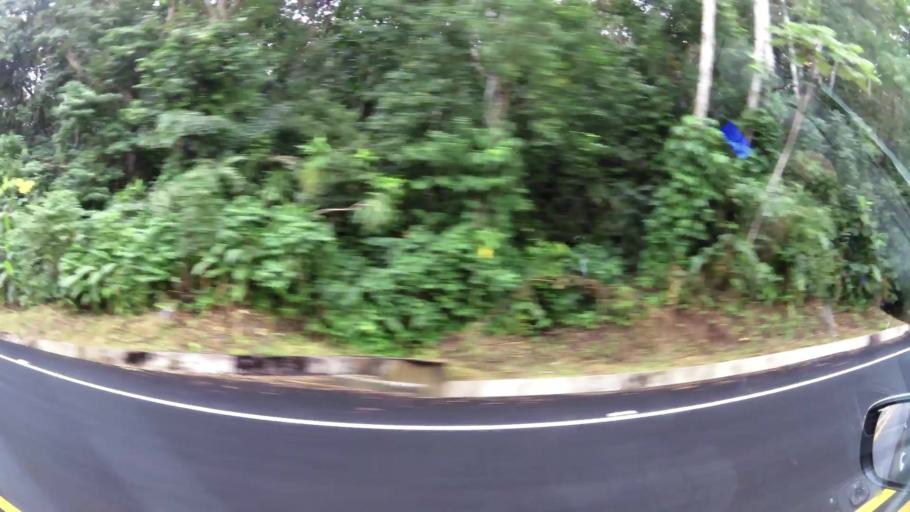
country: CR
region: Alajuela
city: Orotina
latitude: 9.9499
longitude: -84.5705
